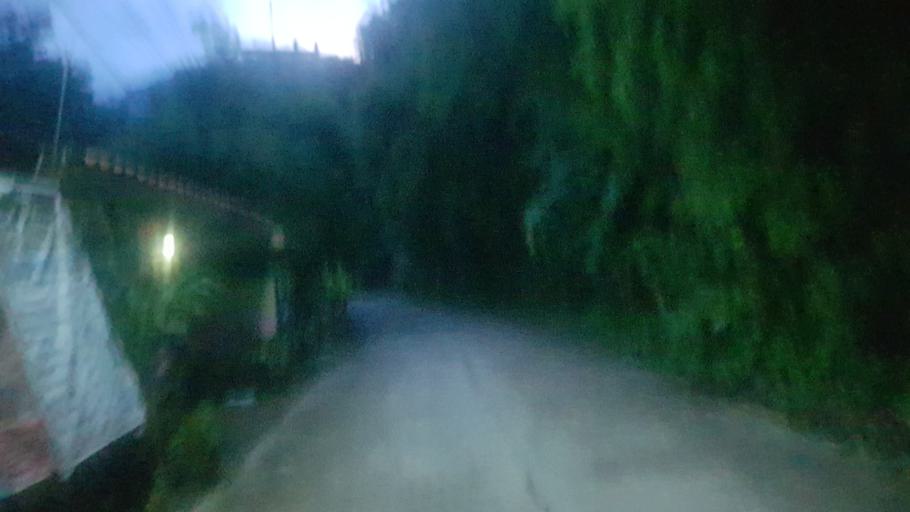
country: TH
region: Phangnga
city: Takua Pa
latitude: 8.9125
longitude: 98.5269
